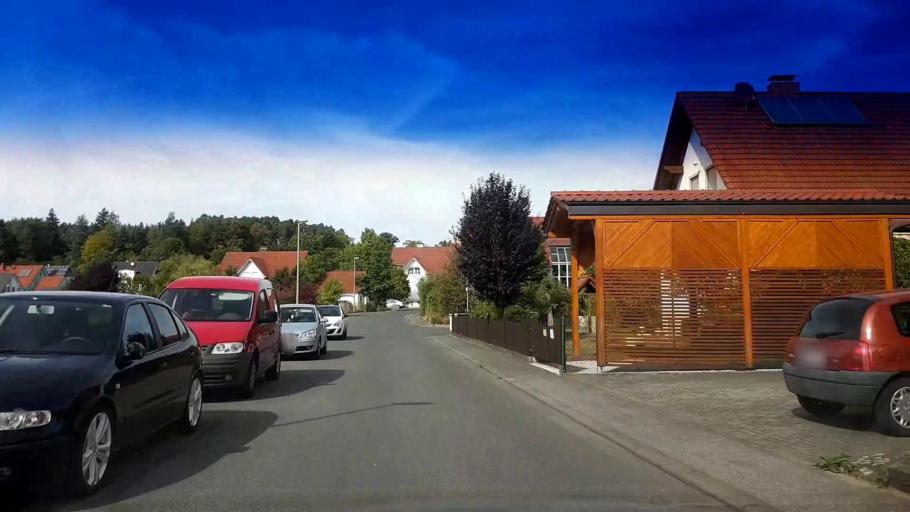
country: DE
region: Bavaria
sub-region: Upper Franconia
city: Oberhaid
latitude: 49.9368
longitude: 10.8062
